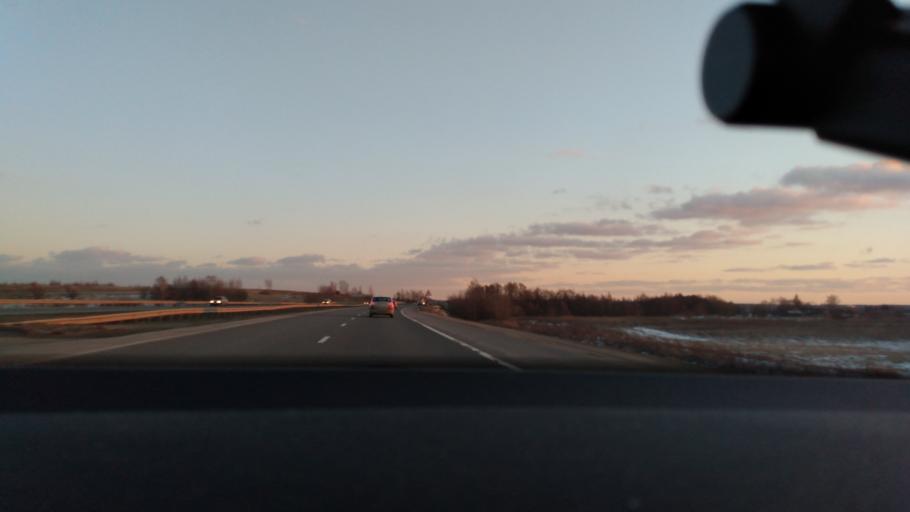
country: RU
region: Moskovskaya
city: Kolomna
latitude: 55.1014
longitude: 38.8987
